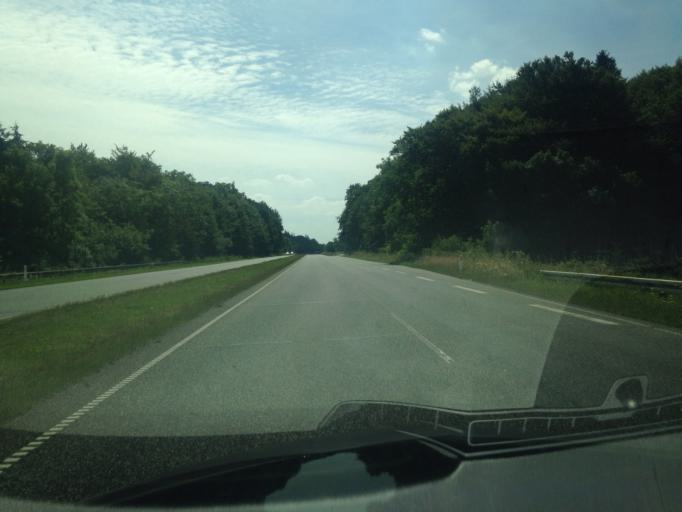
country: DK
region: South Denmark
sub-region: Kolding Kommune
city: Kolding
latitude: 55.5233
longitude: 9.4979
